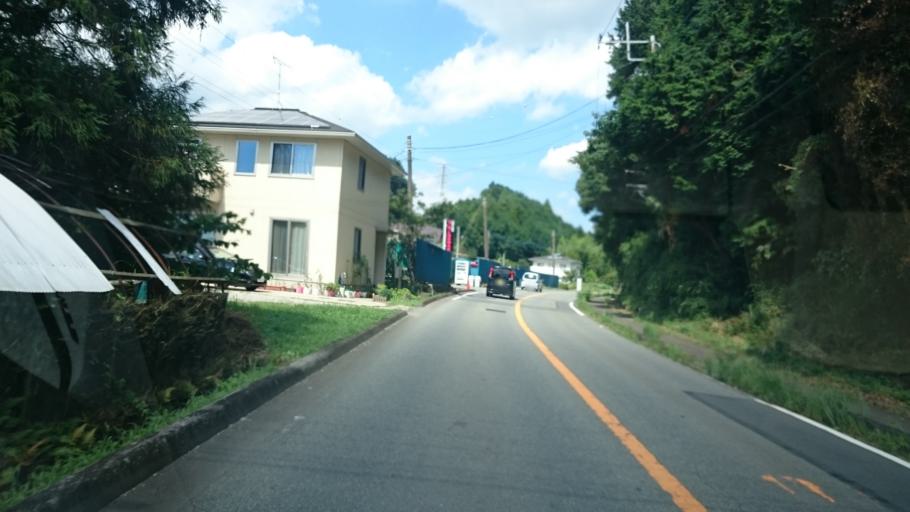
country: JP
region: Shizuoka
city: Mishima
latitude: 35.2009
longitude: 138.9242
